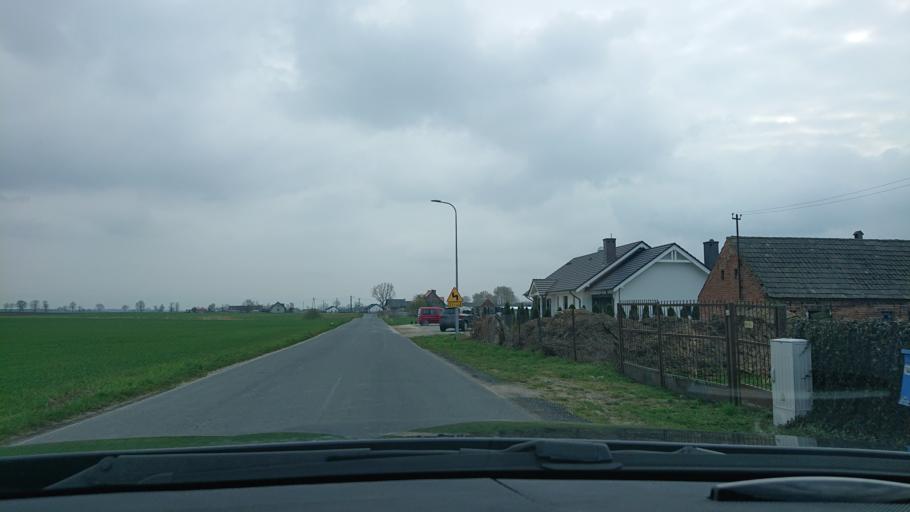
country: PL
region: Greater Poland Voivodeship
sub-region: Powiat gnieznienski
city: Lubowo
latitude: 52.5422
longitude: 17.4944
